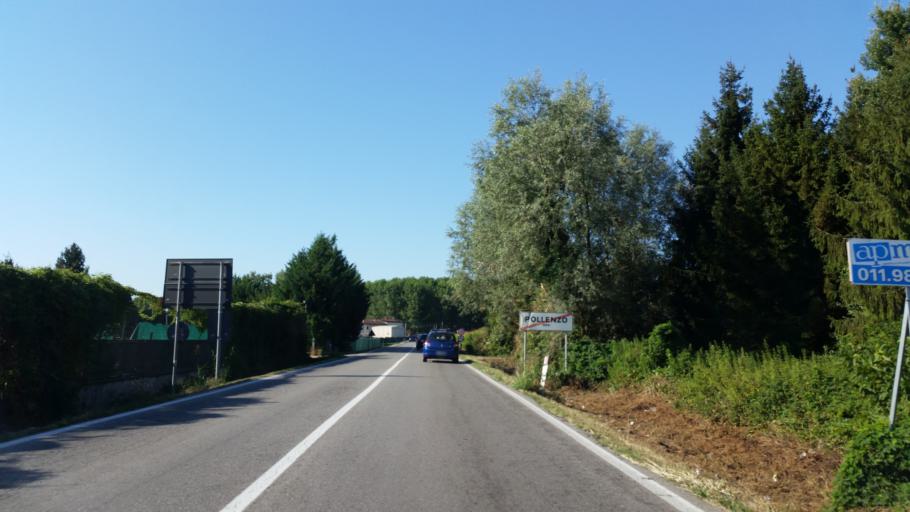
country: IT
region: Piedmont
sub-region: Provincia di Cuneo
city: Cinzano
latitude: 44.6826
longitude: 7.8917
